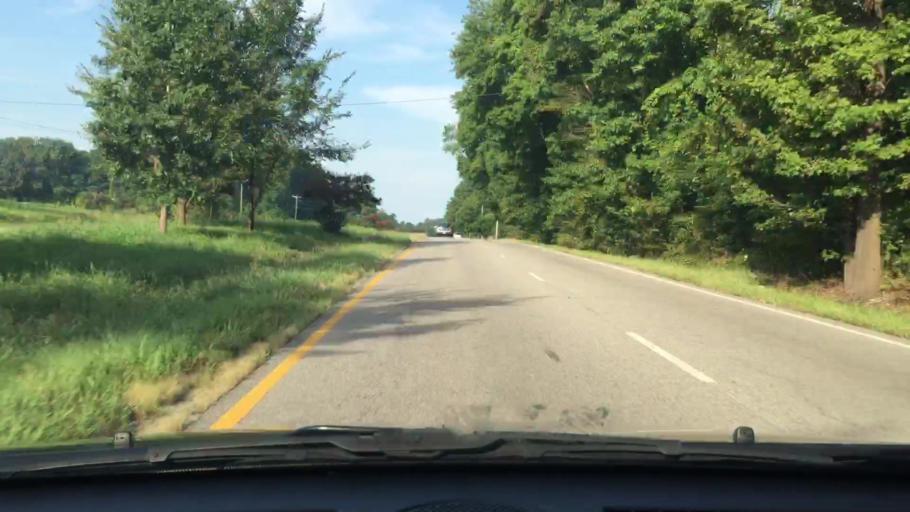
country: US
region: Virginia
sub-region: Isle of Wight County
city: Carrollton
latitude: 36.9423
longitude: -76.5608
